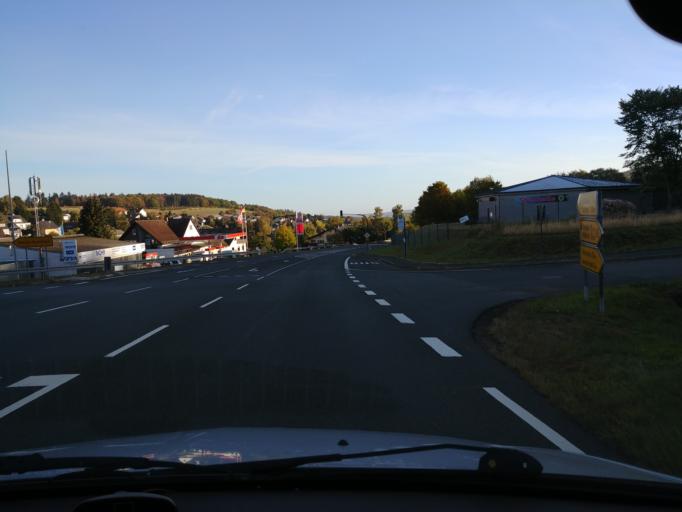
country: DE
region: Hesse
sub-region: Regierungsbezirk Darmstadt
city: Schmitten
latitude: 50.2969
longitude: 8.3879
